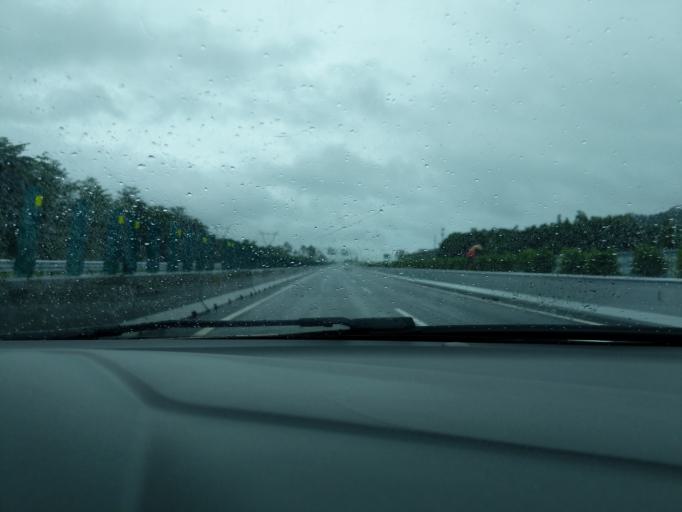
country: CN
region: Guangdong
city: Pingshi
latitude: 22.2529
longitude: 112.3085
